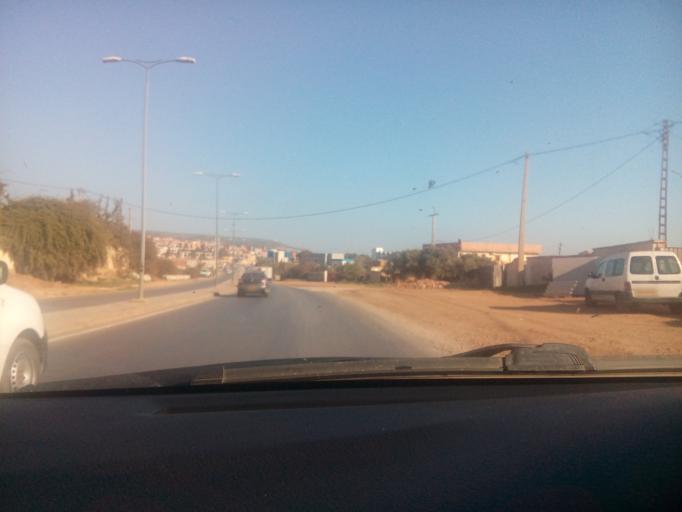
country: DZ
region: Oran
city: Oran
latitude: 35.6542
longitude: -0.6984
